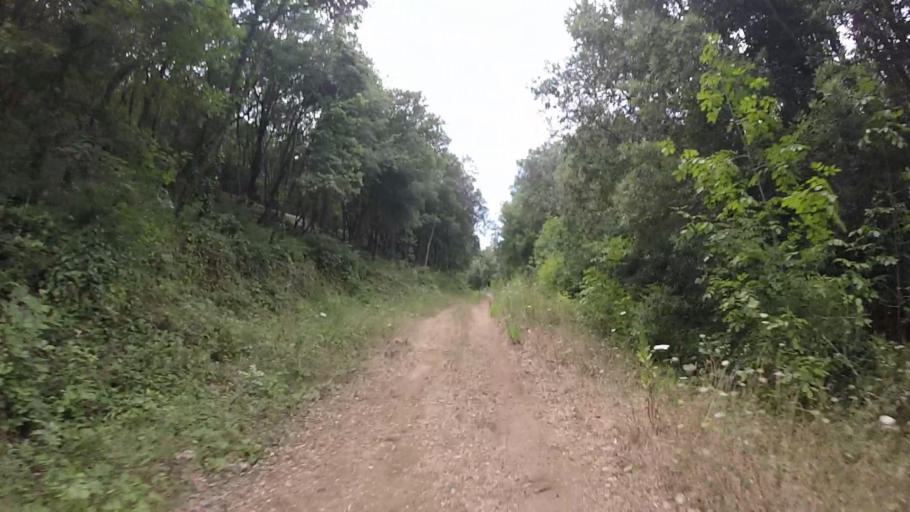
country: FR
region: Provence-Alpes-Cote d'Azur
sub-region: Departement des Alpes-Maritimes
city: Biot
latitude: 43.6169
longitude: 7.0885
